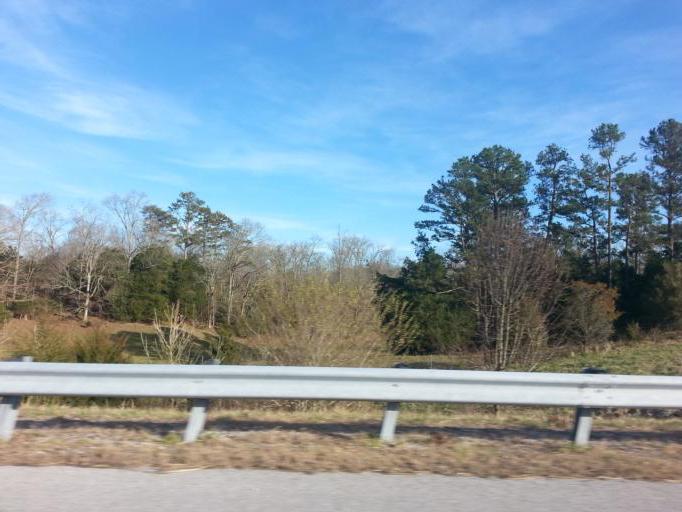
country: US
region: Tennessee
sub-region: White County
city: Sparta
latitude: 35.8449
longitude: -85.5081
